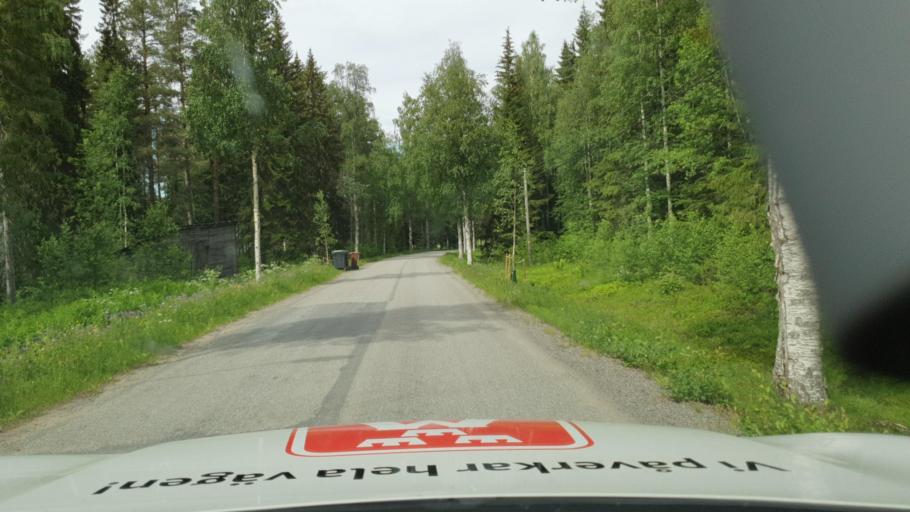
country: SE
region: Vaesterbotten
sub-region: Skelleftea Kommun
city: Burtraesk
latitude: 64.4447
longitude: 20.4845
